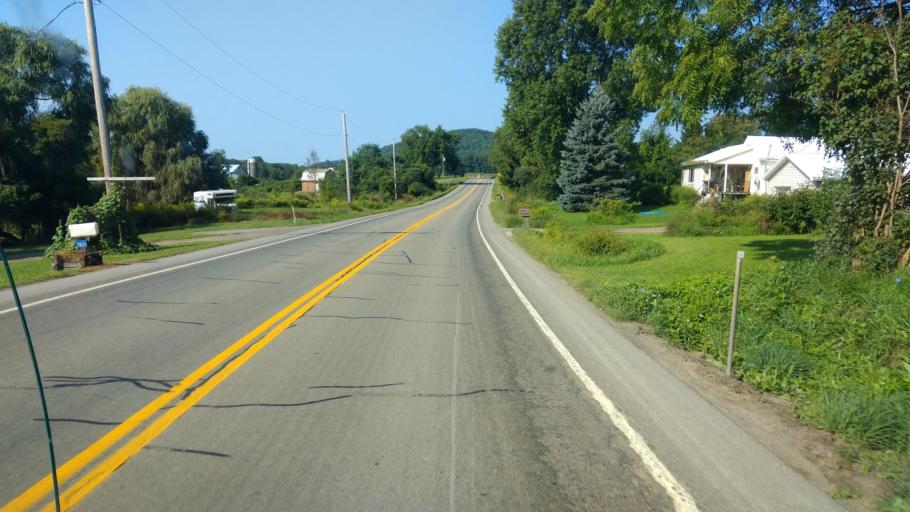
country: US
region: New York
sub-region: Allegany County
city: Friendship
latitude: 42.3028
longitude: -78.1817
